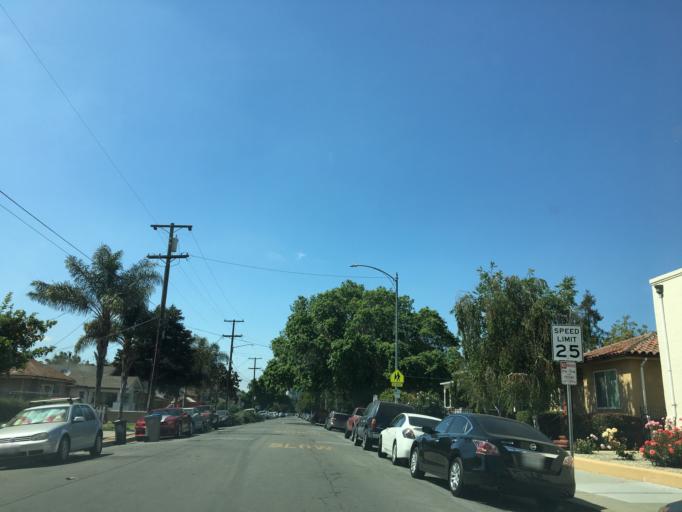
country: US
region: California
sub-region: Santa Clara County
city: San Jose
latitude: 37.3175
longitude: -121.8852
